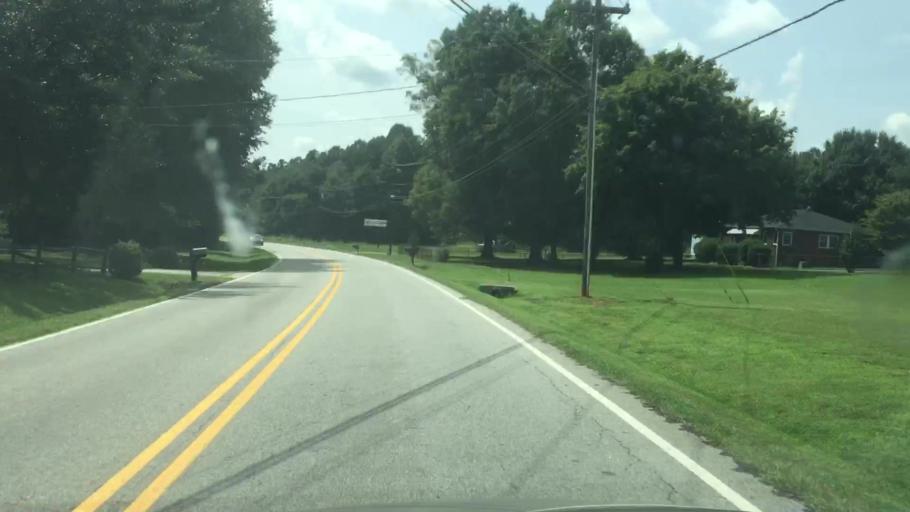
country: US
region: North Carolina
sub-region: Rowan County
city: China Grove
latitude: 35.6526
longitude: -80.5910
